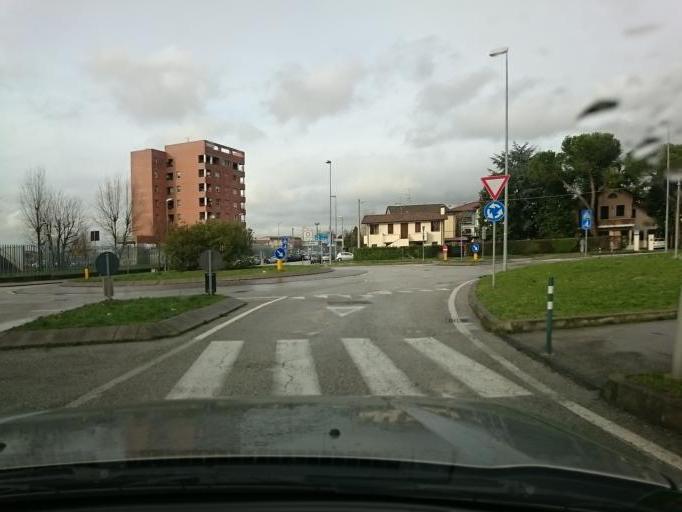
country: IT
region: Veneto
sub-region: Provincia di Padova
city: Padova
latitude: 45.4129
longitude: 11.8968
